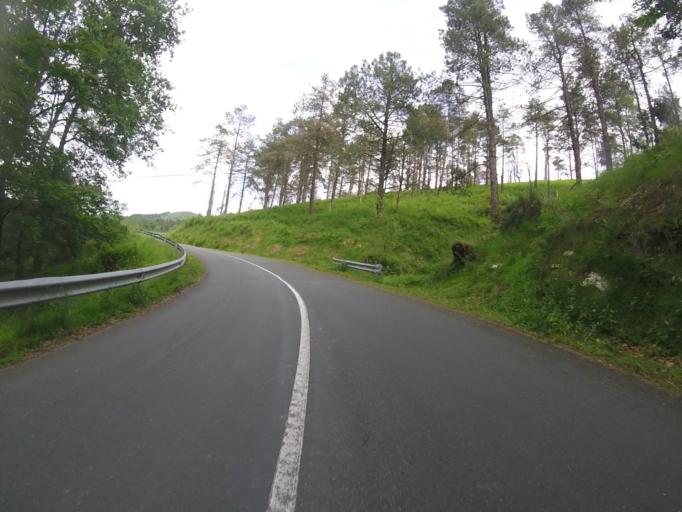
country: ES
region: Navarre
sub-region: Provincia de Navarra
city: Arano
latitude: 43.2447
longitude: -1.8445
